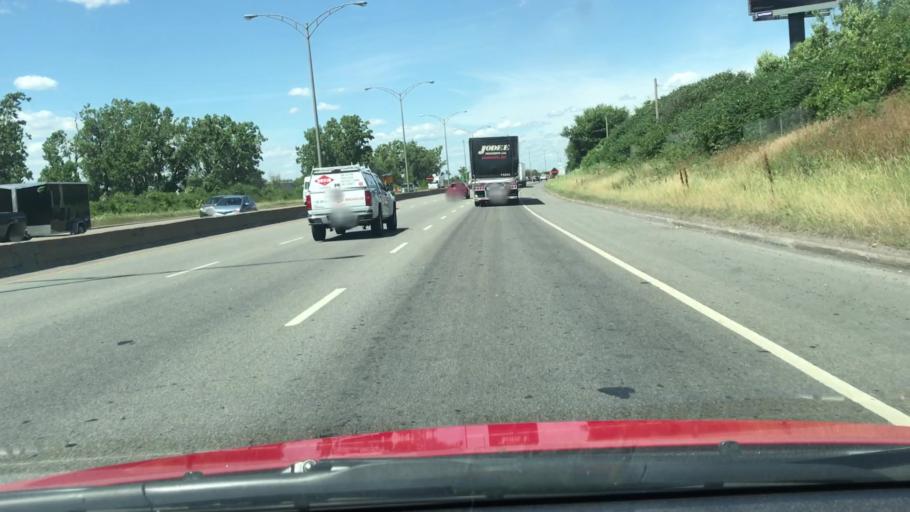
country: CA
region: Quebec
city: Cote-Saint-Luc
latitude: 45.4558
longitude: -73.6971
